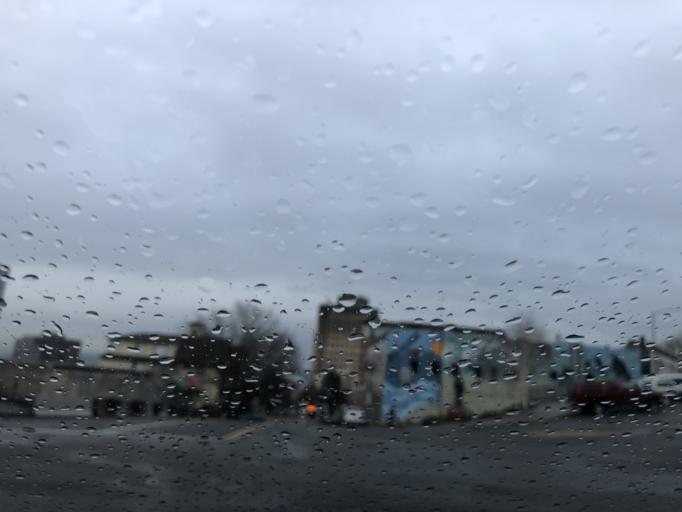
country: US
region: Washington
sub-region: Pierce County
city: Tacoma
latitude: 47.2587
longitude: -122.4434
